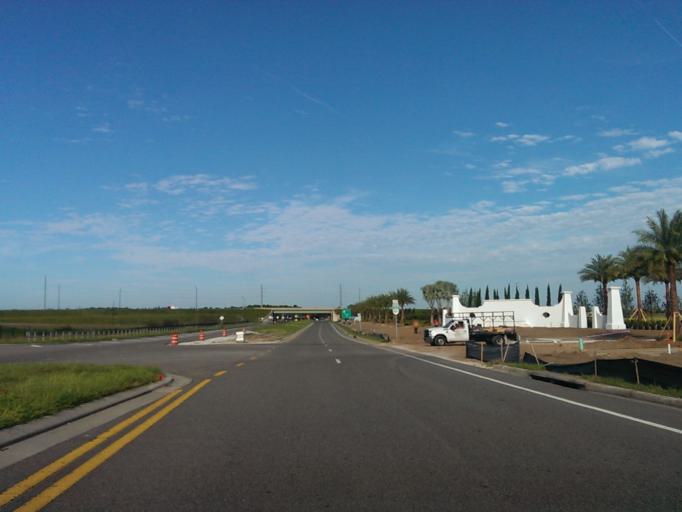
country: US
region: Florida
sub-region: Polk County
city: Citrus Ridge
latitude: 28.4198
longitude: -81.6279
